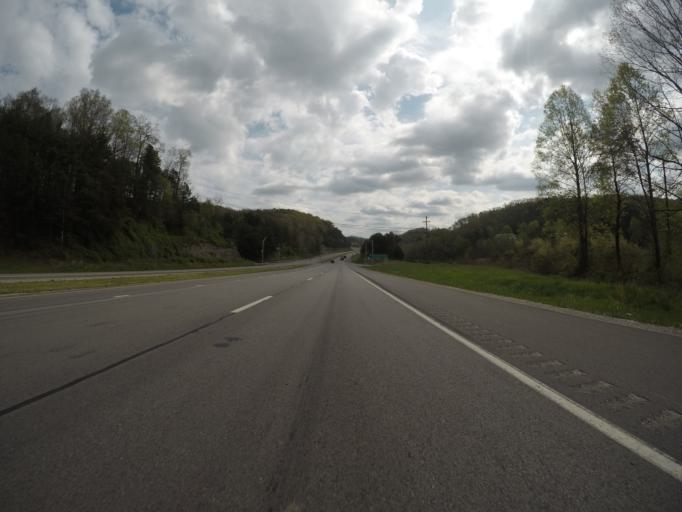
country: US
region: West Virginia
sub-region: Kanawha County
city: Alum Creek
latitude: 38.2775
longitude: -81.7764
